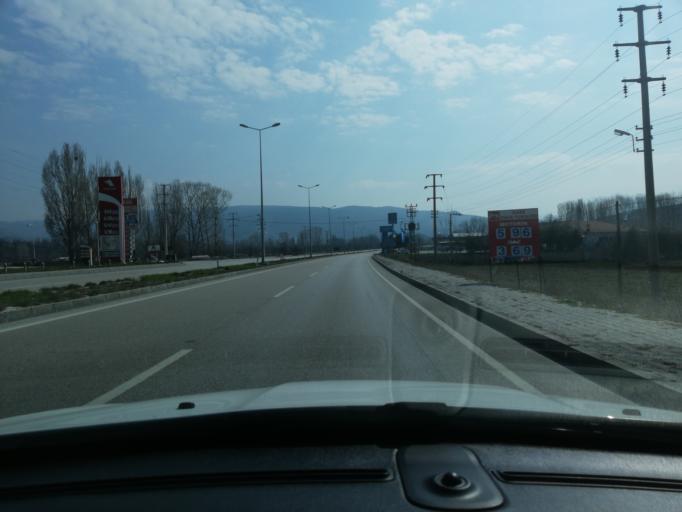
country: TR
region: Cankiri
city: Ilgaz
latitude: 40.9085
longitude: 33.6297
